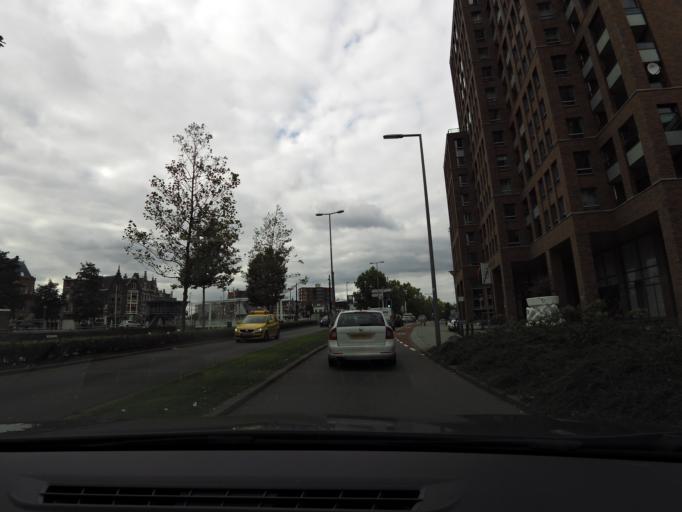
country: NL
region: South Holland
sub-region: Gemeente Rotterdam
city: Delfshaven
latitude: 51.9094
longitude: 4.4507
